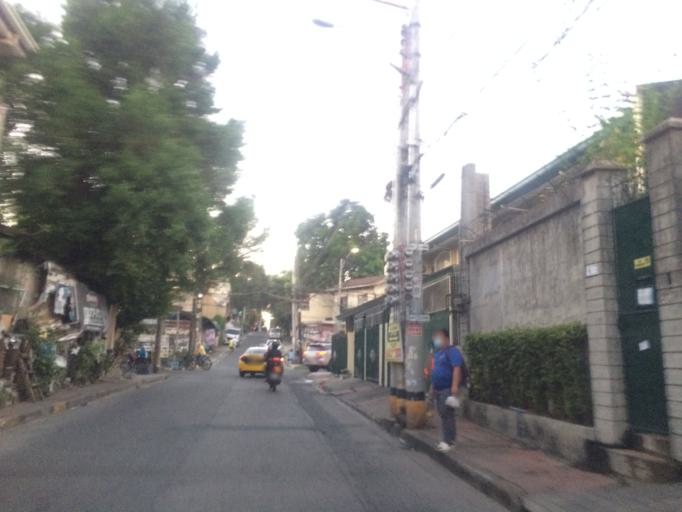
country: PH
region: Calabarzon
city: Del Monte
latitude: 14.6428
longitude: 121.0141
